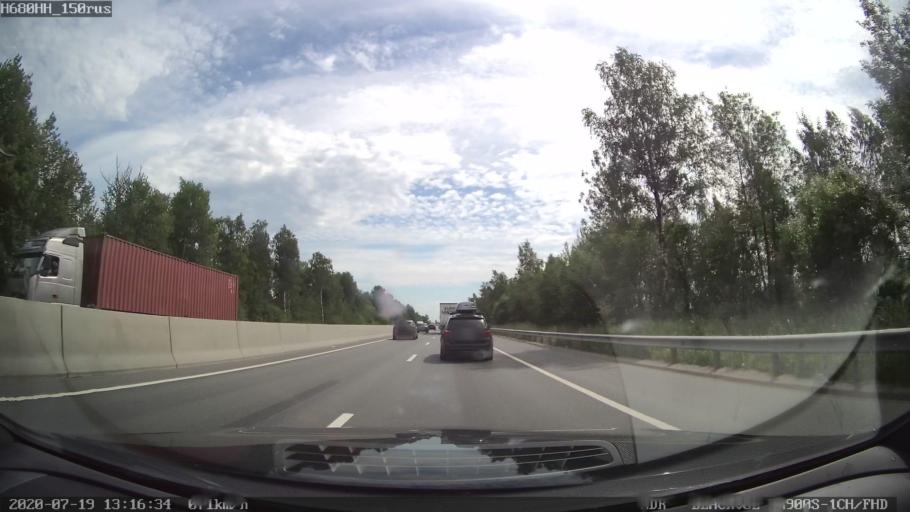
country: RU
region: St.-Petersburg
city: Kolpino
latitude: 59.7161
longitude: 30.5566
